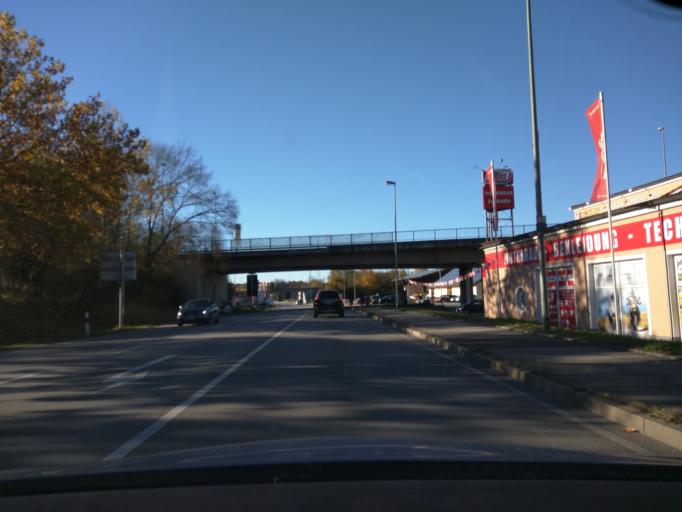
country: DE
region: Bavaria
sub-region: Lower Bavaria
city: Passau
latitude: 48.5748
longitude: 13.4147
